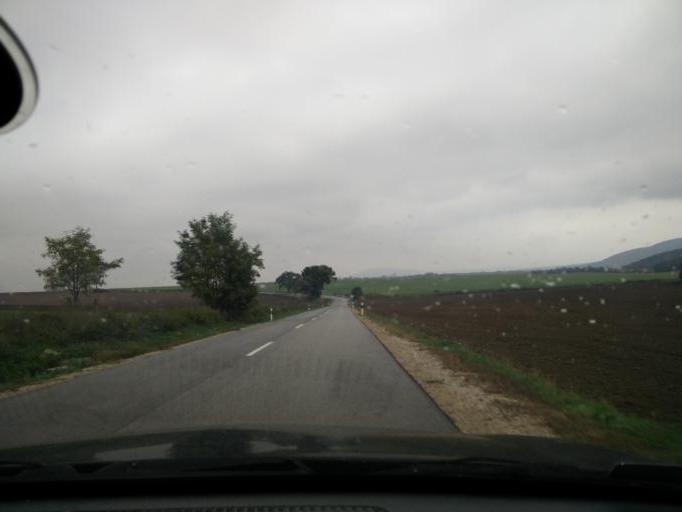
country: HU
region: Komarom-Esztergom
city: Bajna
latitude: 47.6362
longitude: 18.5686
